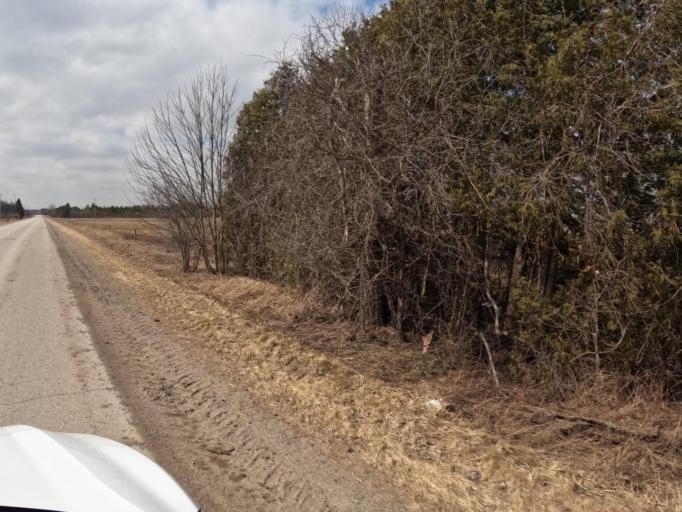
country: CA
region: Ontario
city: Shelburne
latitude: 44.0178
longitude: -80.1694
